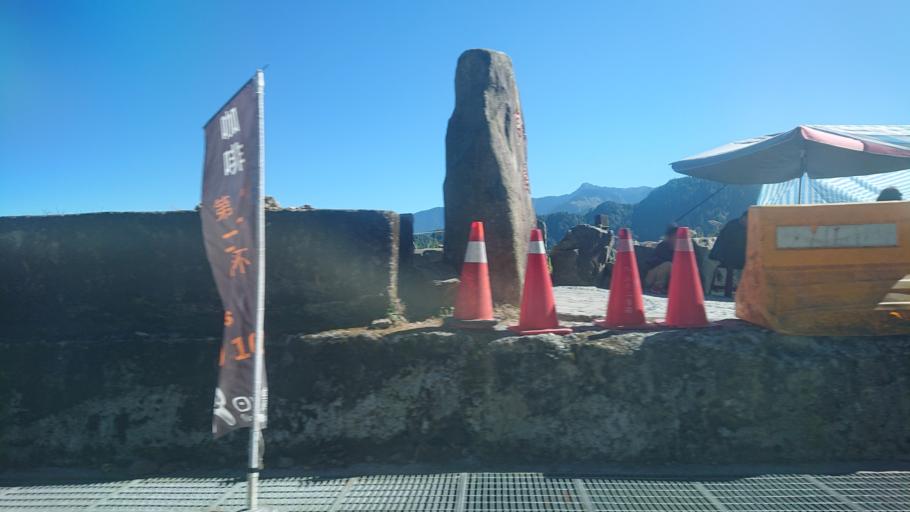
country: TW
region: Taiwan
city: Lugu
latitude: 23.4836
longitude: 120.8304
